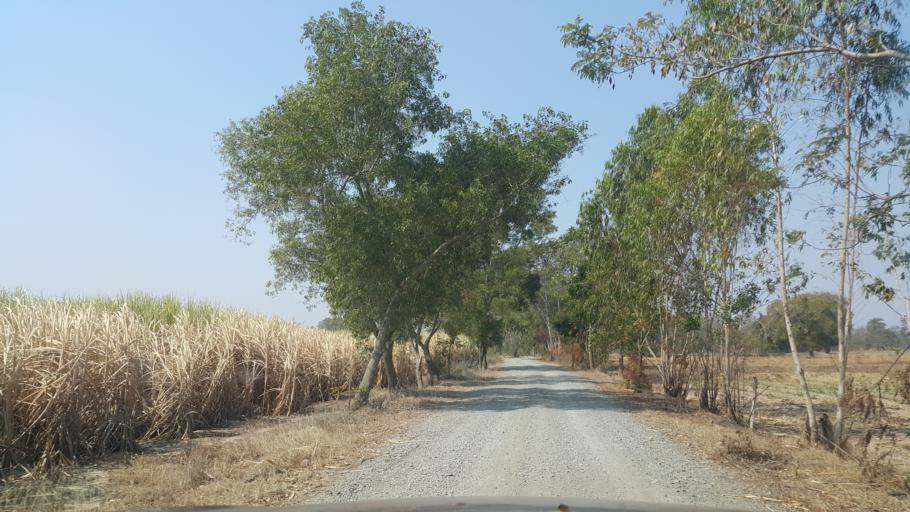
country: TH
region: Buriram
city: Krasang
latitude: 15.0909
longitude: 103.3783
